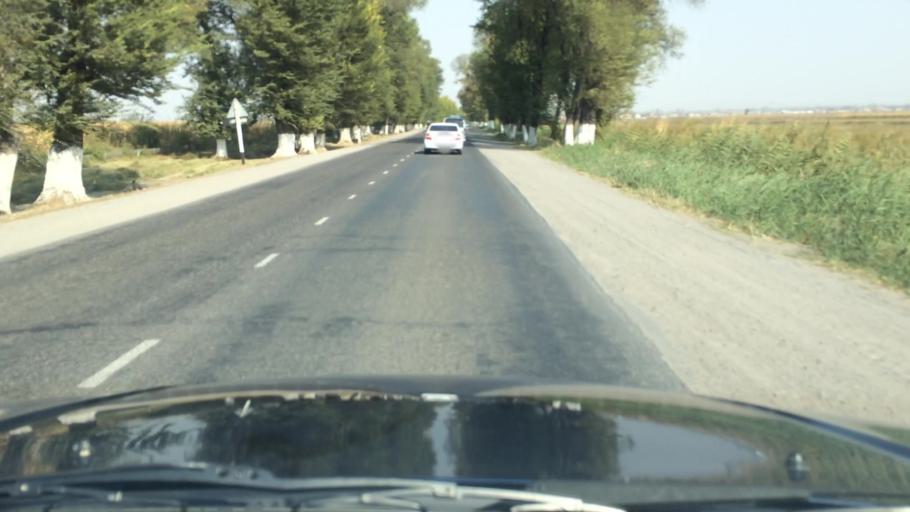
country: KG
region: Chuy
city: Lebedinovka
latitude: 42.9018
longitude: 74.6855
